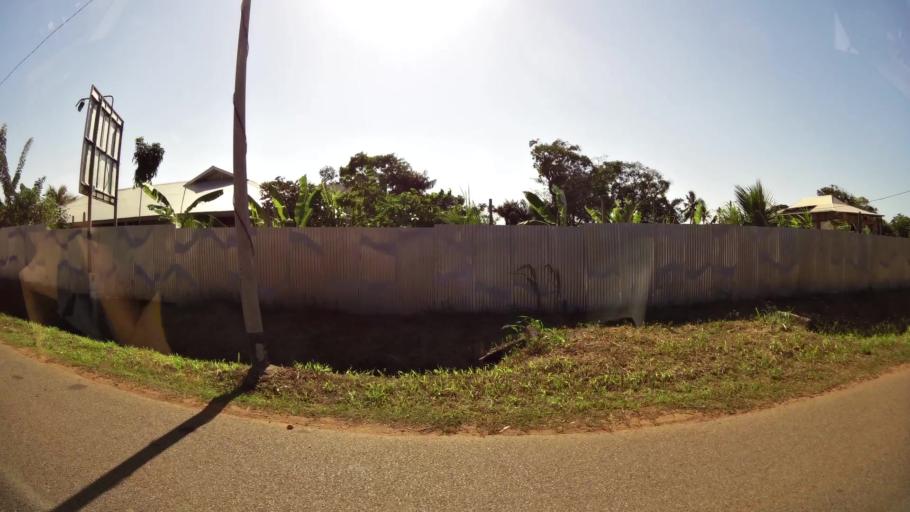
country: GF
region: Guyane
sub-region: Guyane
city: Remire-Montjoly
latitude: 4.8931
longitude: -52.2739
